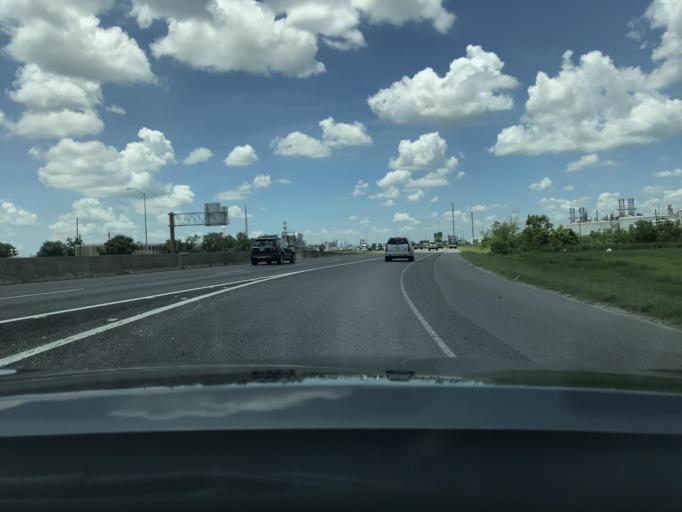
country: US
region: Louisiana
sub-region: Calcasieu Parish
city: Westlake
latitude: 30.2374
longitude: -93.2635
